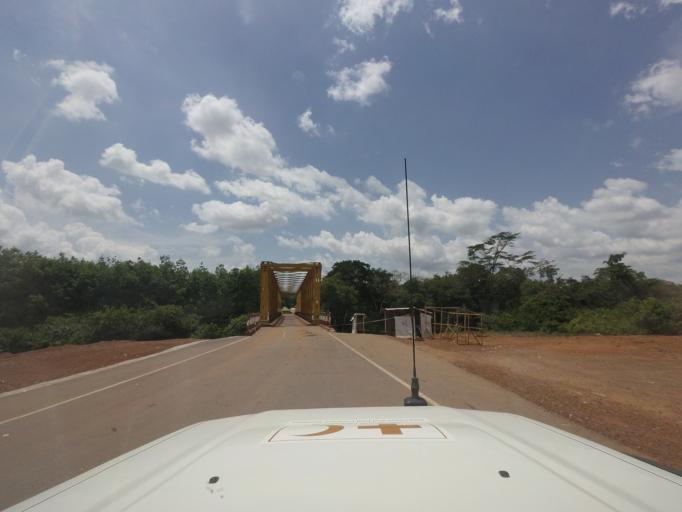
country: LR
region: Nimba
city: Sanniquellie
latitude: 7.2509
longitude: -8.9834
